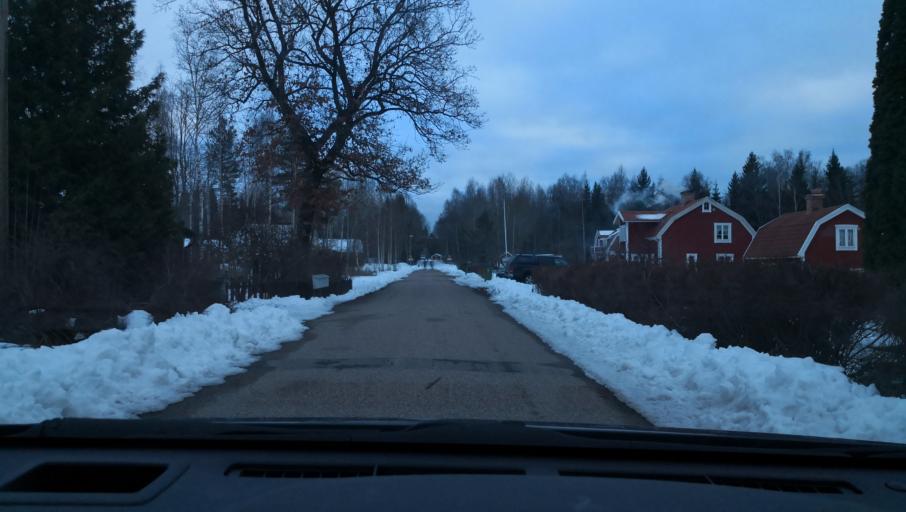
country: SE
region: Dalarna
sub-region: Smedjebackens Kommun
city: Smedjebacken
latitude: 60.0651
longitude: 15.5535
